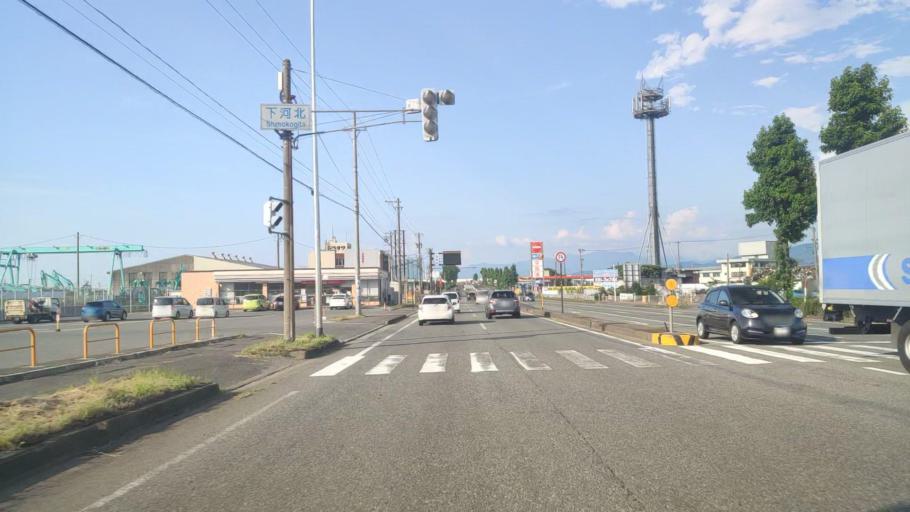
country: JP
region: Fukui
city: Fukui-shi
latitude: 36.0208
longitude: 136.2142
